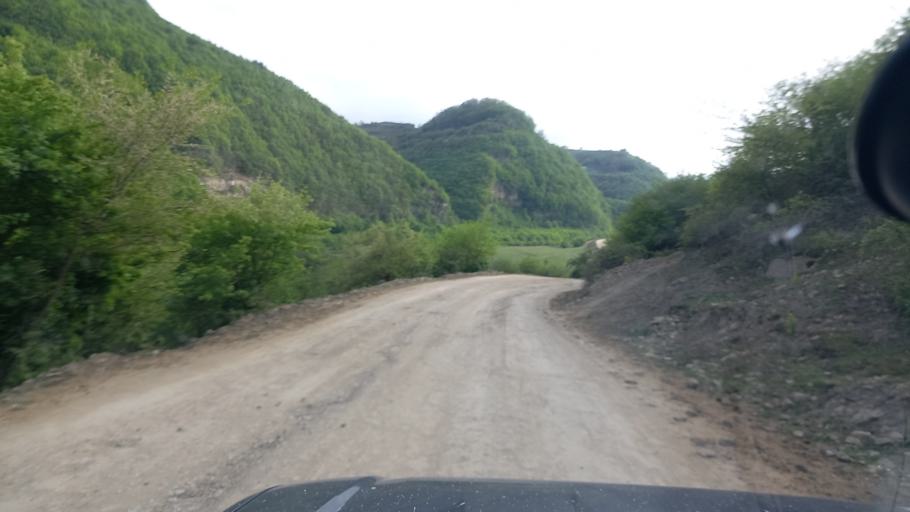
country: RU
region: Dagestan
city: Khuchni
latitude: 41.9655
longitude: 47.8731
